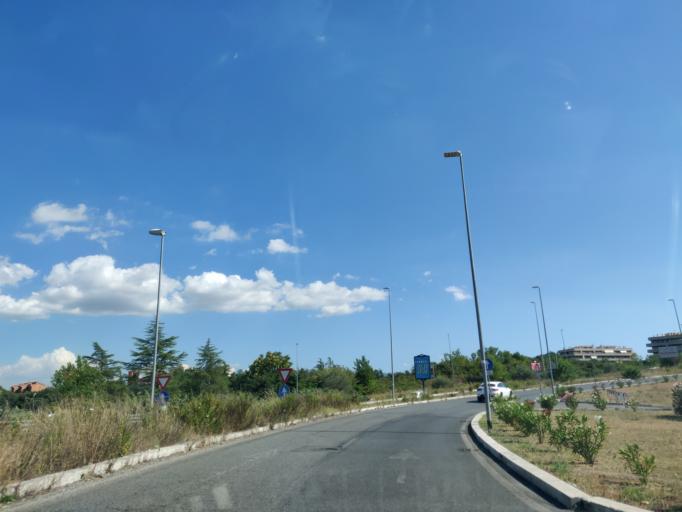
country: IT
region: Latium
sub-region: Citta metropolitana di Roma Capitale
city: Setteville
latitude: 41.9139
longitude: 12.6639
